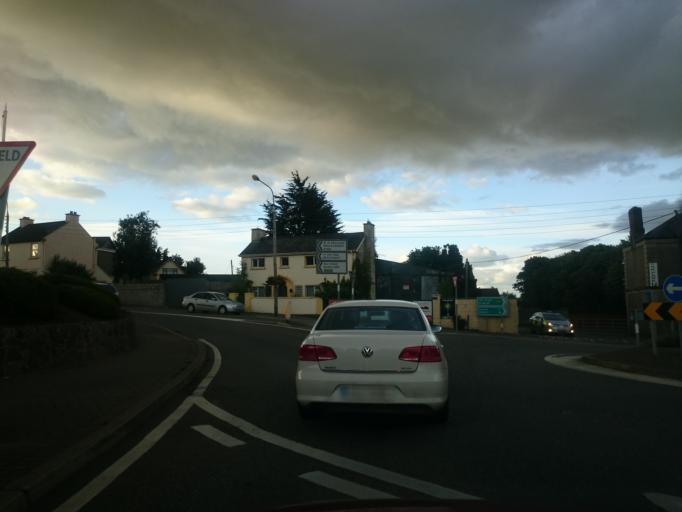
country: IE
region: Leinster
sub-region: Loch Garman
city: Ferns
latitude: 52.5899
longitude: -6.4965
